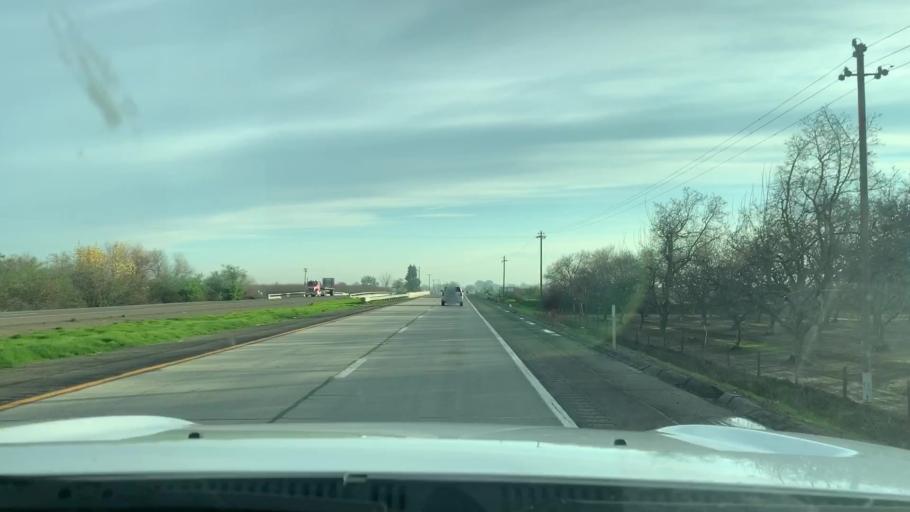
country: US
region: California
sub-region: Fresno County
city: Riverdale
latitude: 36.3876
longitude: -119.8098
